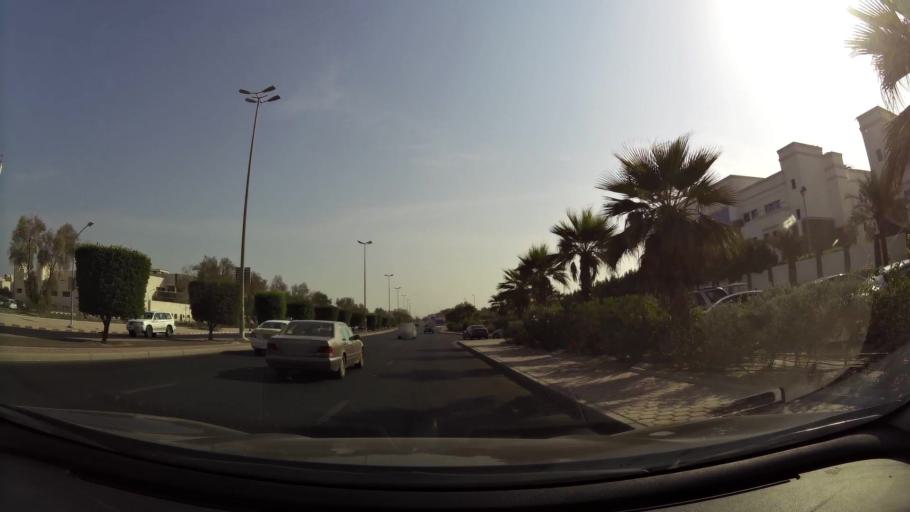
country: KW
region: Al Ahmadi
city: Ar Riqqah
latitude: 29.1639
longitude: 48.1018
